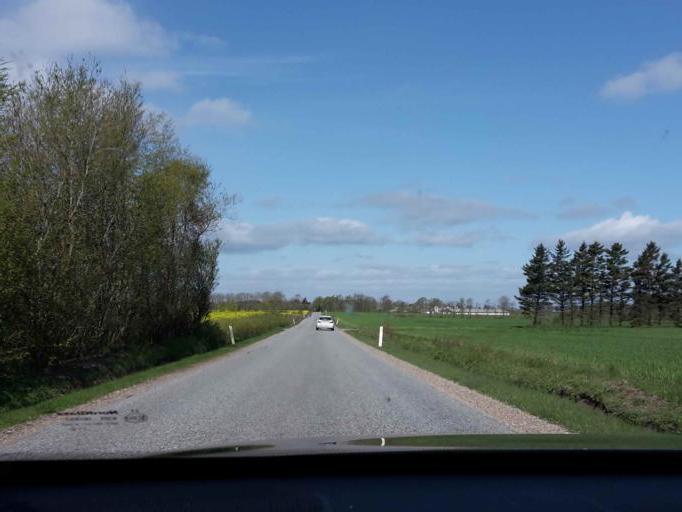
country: DK
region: South Denmark
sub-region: Vejen Kommune
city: Holsted
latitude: 55.5820
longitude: 8.9726
